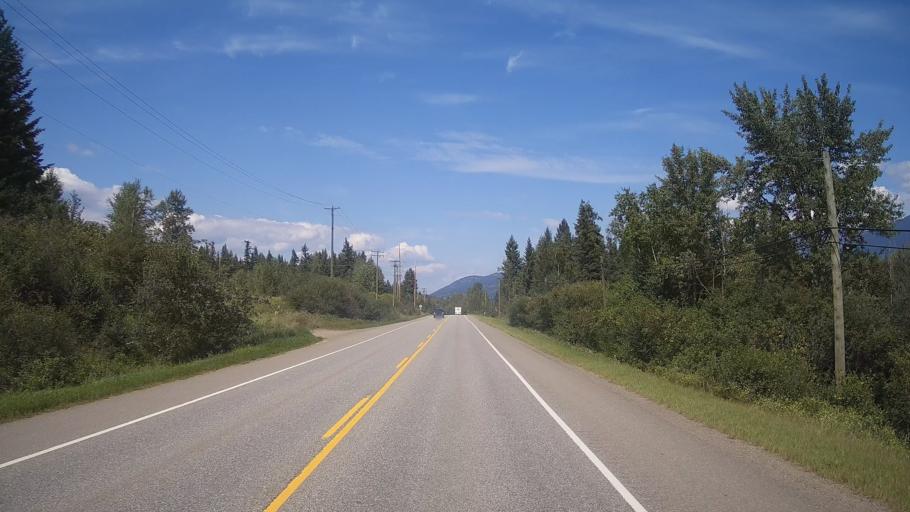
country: CA
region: British Columbia
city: Kamloops
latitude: 51.3104
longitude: -120.1808
